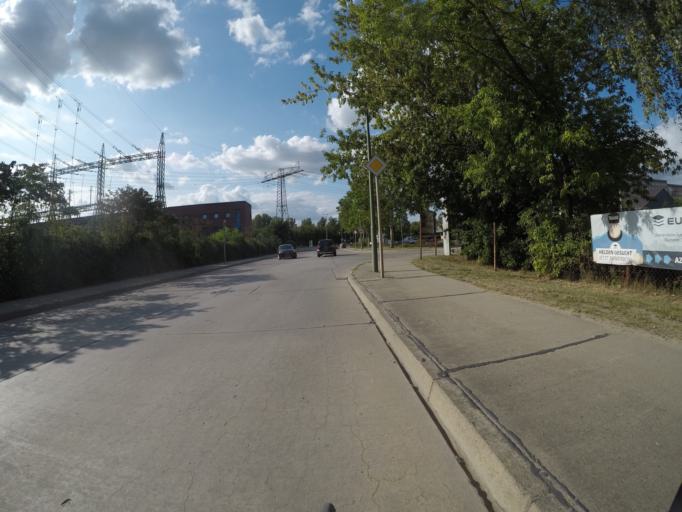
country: DE
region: Berlin
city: Alt-Hohenschoenhausen
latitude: 52.5352
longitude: 13.5255
